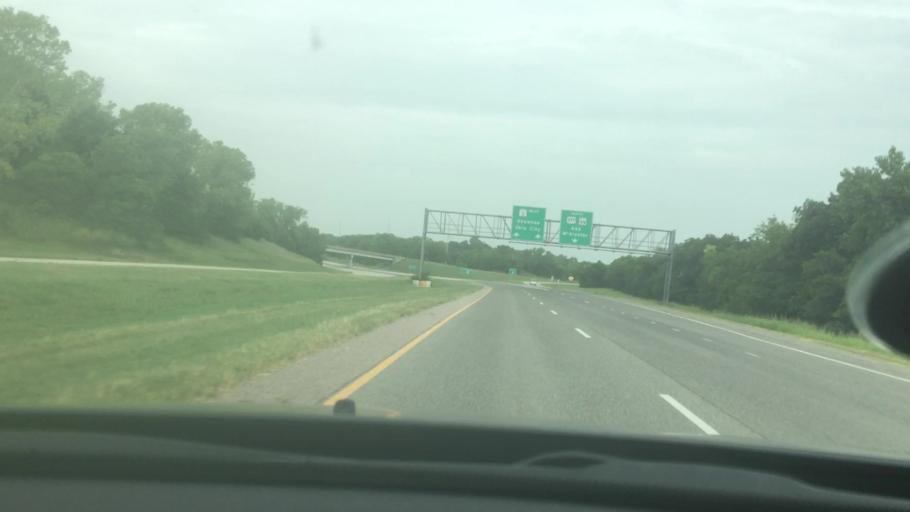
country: US
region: Oklahoma
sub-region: Pontotoc County
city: Ada
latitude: 34.7473
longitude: -96.6532
